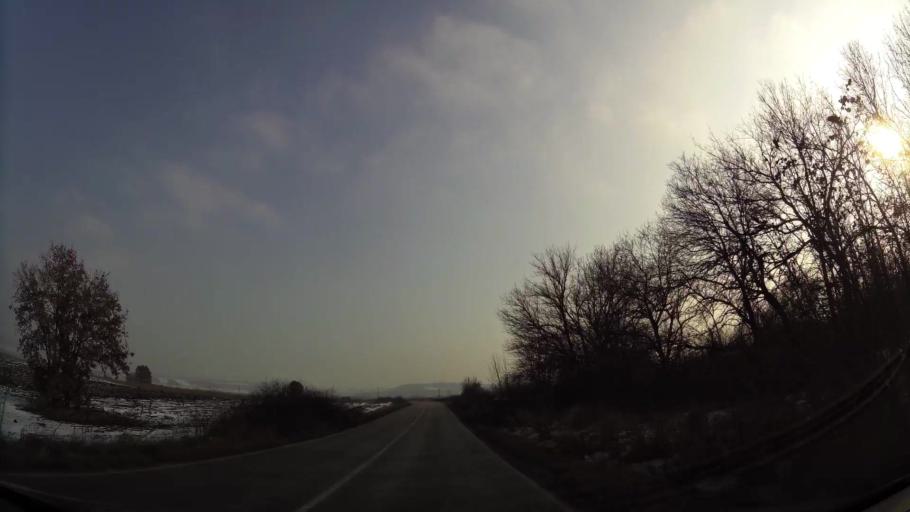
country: MK
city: Miladinovci
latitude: 41.9744
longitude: 21.6320
